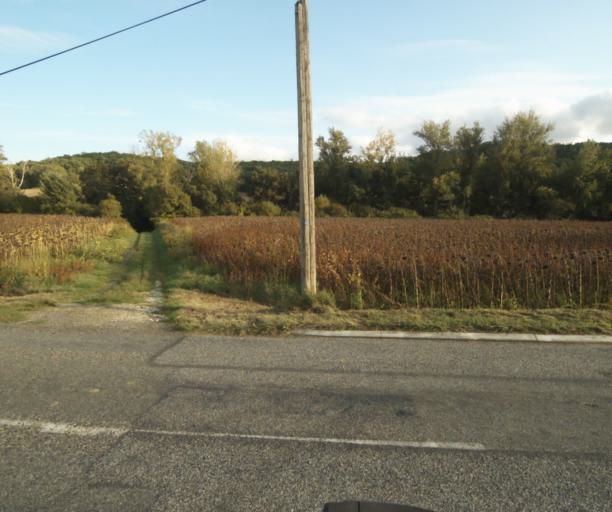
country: FR
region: Midi-Pyrenees
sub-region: Departement de la Haute-Garonne
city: Launac
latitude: 43.8174
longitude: 1.1264
